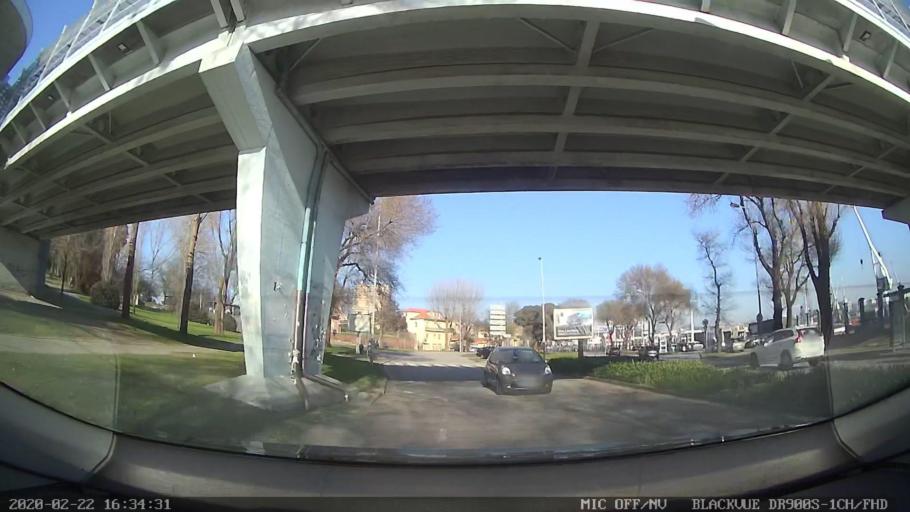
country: PT
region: Porto
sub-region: Matosinhos
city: Leca da Palmeira
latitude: 41.1899
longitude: -8.6957
